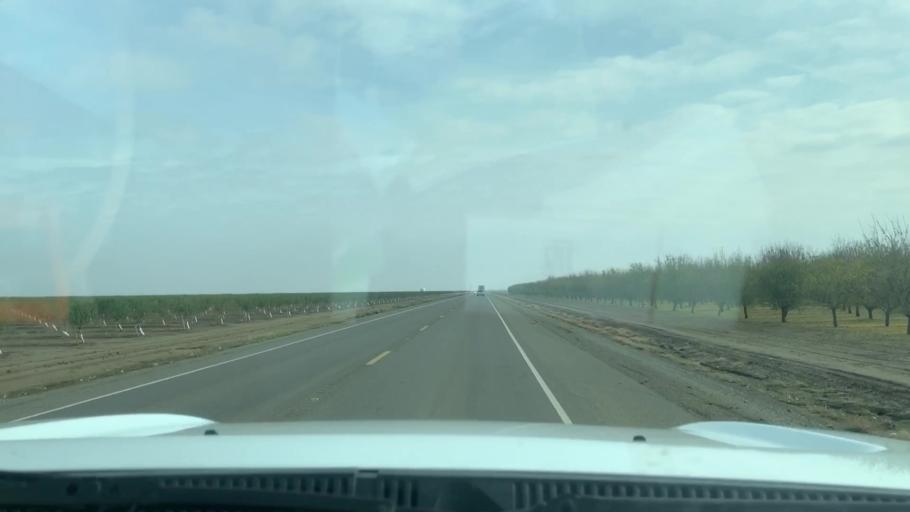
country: US
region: California
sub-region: Kings County
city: Lemoore Station
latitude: 36.2554
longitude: -120.0091
